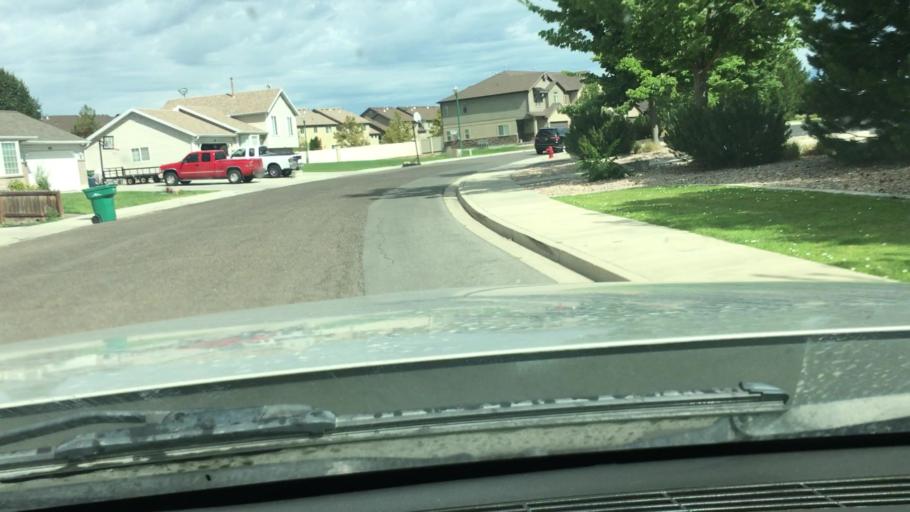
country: US
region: Utah
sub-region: Utah County
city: Orem
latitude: 40.2807
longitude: -111.7391
